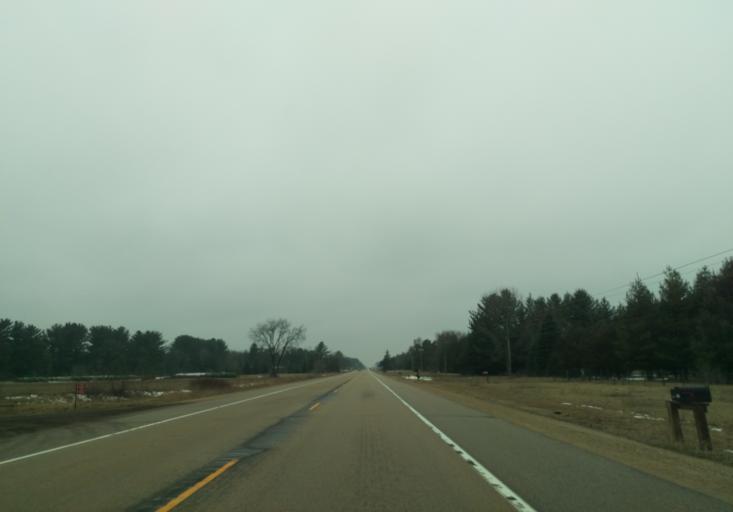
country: US
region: Wisconsin
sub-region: Sauk County
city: Spring Green
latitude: 43.1615
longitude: -89.9365
